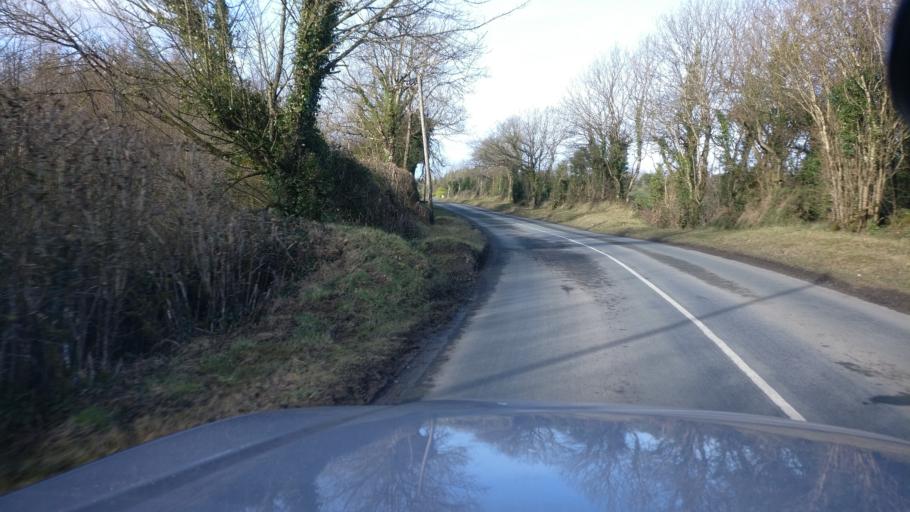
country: IE
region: Leinster
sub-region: Laois
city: Stradbally
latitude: 52.9361
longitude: -7.1962
